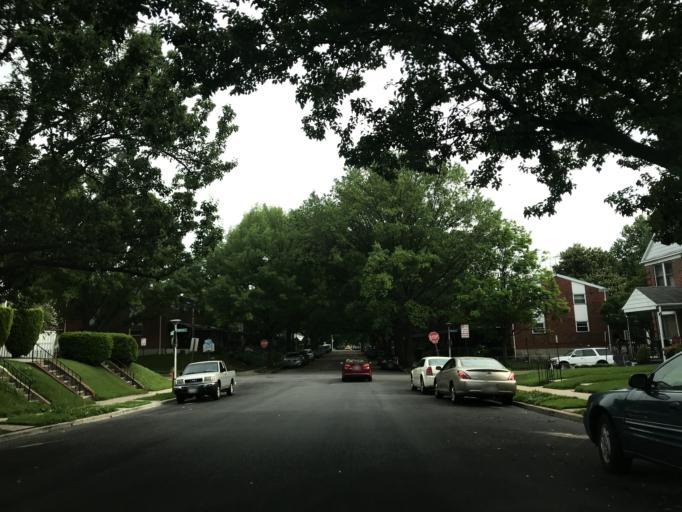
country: US
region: Maryland
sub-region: City of Baltimore
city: Baltimore
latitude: 39.3131
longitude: -76.6614
